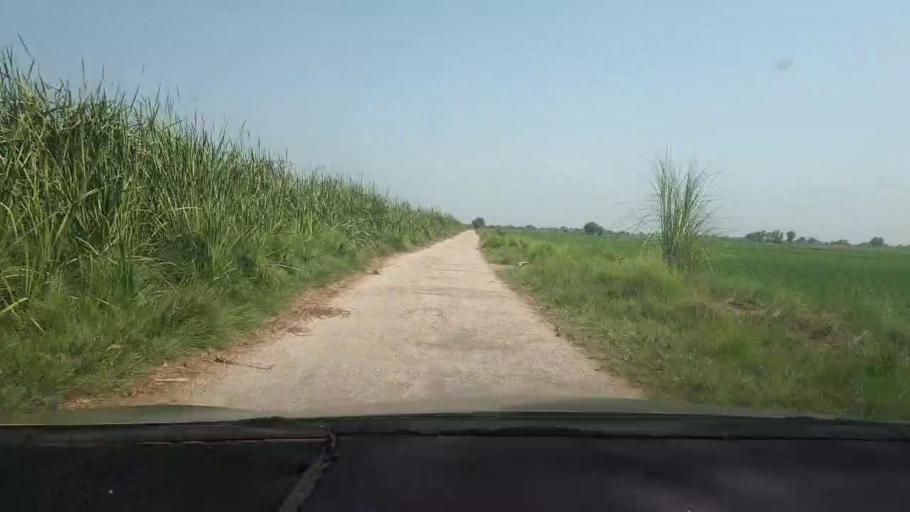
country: PK
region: Sindh
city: Miro Khan
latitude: 27.7010
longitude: 68.0908
